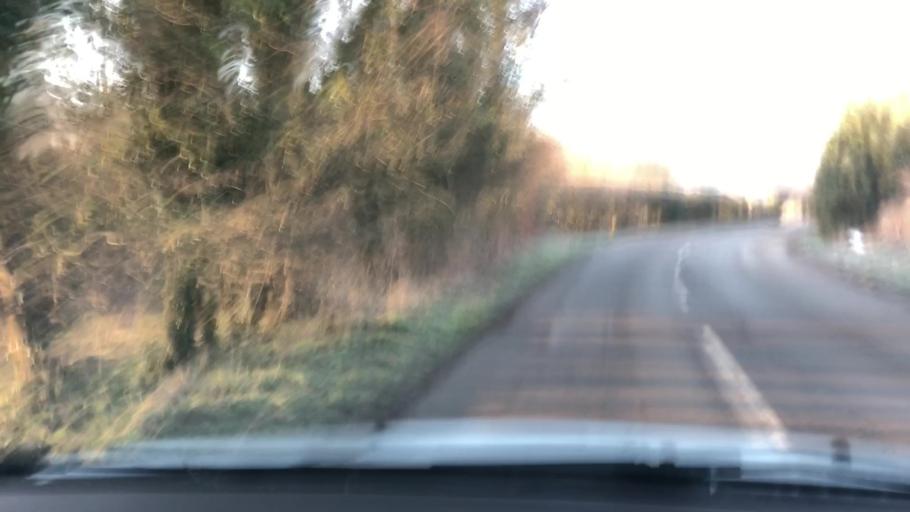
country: GB
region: England
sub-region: Hampshire
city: Alton
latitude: 51.1867
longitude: -1.0174
